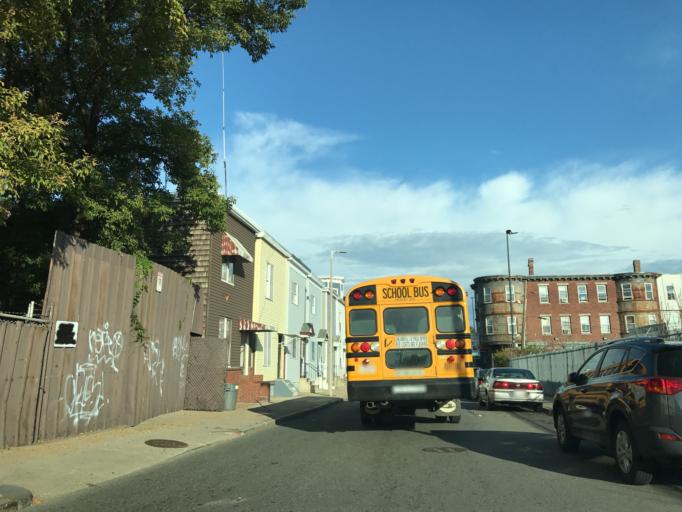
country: US
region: Massachusetts
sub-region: Suffolk County
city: South Boston
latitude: 42.3216
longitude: -71.0660
